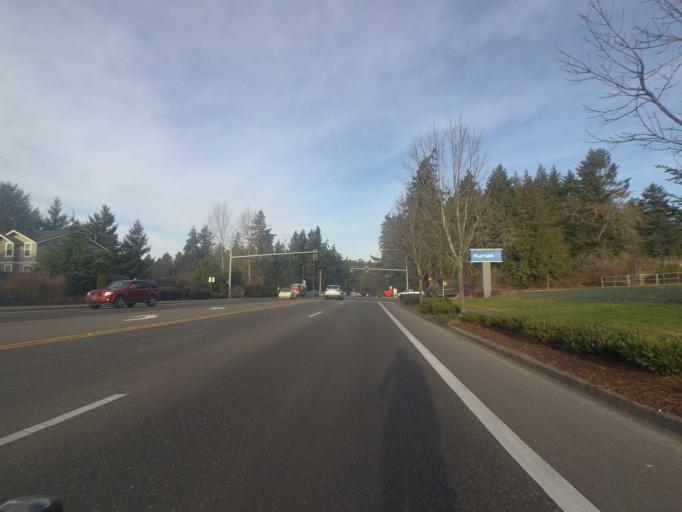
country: US
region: Washington
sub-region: Pierce County
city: Lakewood
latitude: 47.1943
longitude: -122.5202
